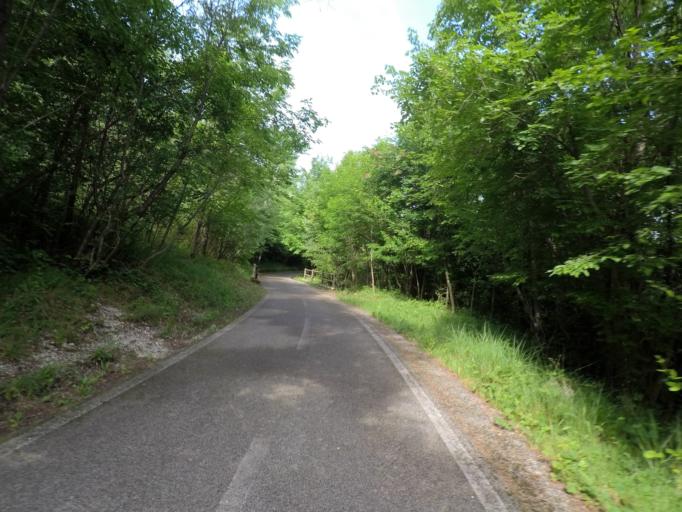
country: IT
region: Friuli Venezia Giulia
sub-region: Provincia di Udine
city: Amaro
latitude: 46.3604
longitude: 13.0906
